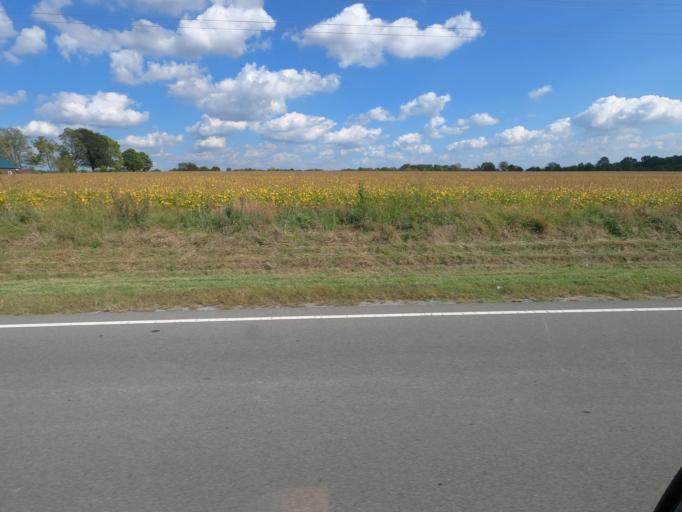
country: US
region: Illinois
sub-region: Massac County
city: Metropolis
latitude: 37.1784
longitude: -88.6767
